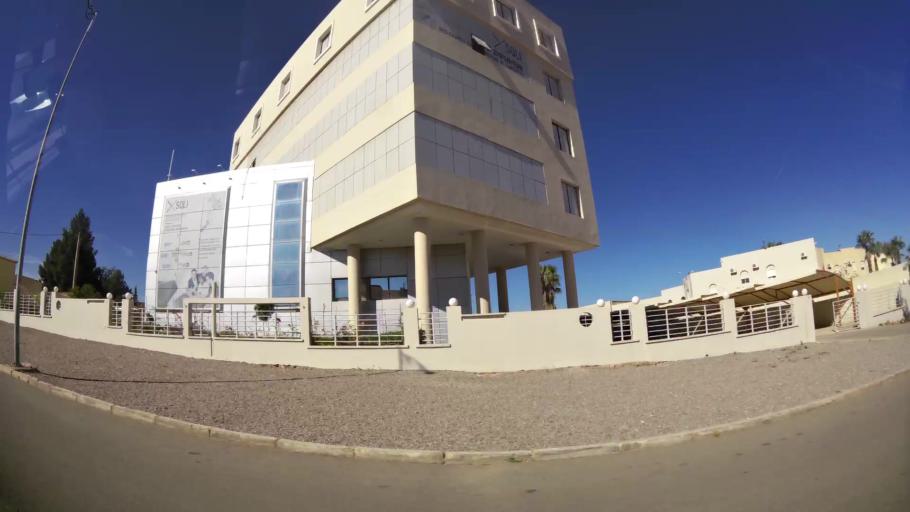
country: MA
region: Oriental
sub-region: Oujda-Angad
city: Oujda
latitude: 34.6514
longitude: -1.8956
